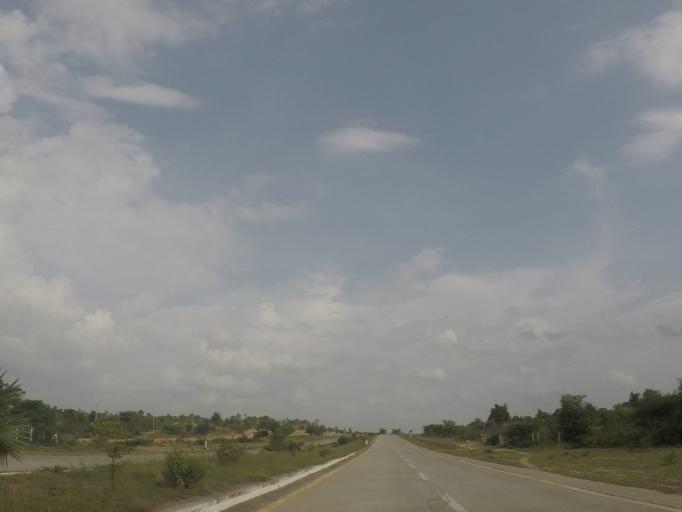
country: MM
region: Mandalay
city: Meiktila
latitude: 20.7055
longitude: 95.7901
